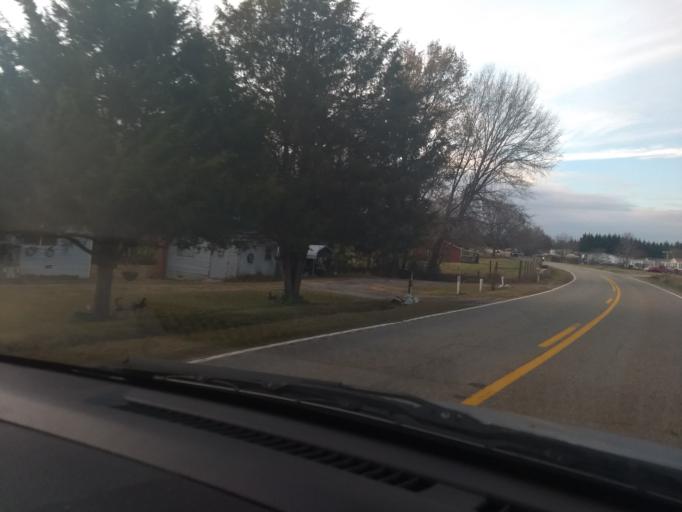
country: US
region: South Carolina
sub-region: Greenville County
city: Greer
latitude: 34.9915
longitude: -82.2031
